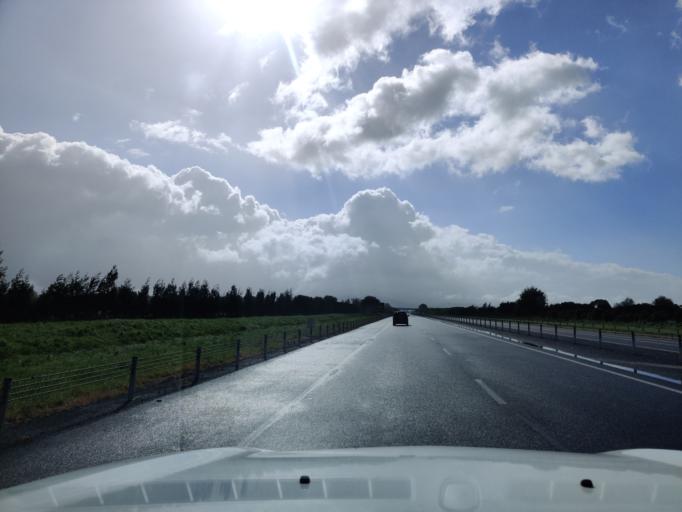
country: NZ
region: Waikato
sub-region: Waipa District
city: Cambridge
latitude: -37.8685
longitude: 175.4280
